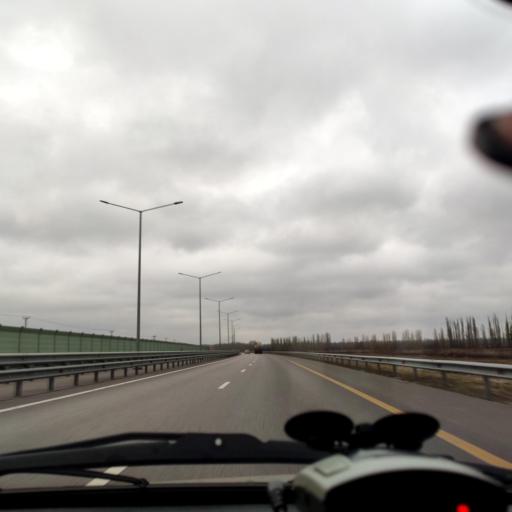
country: RU
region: Voronezj
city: Novaya Usman'
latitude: 51.5897
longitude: 39.3761
